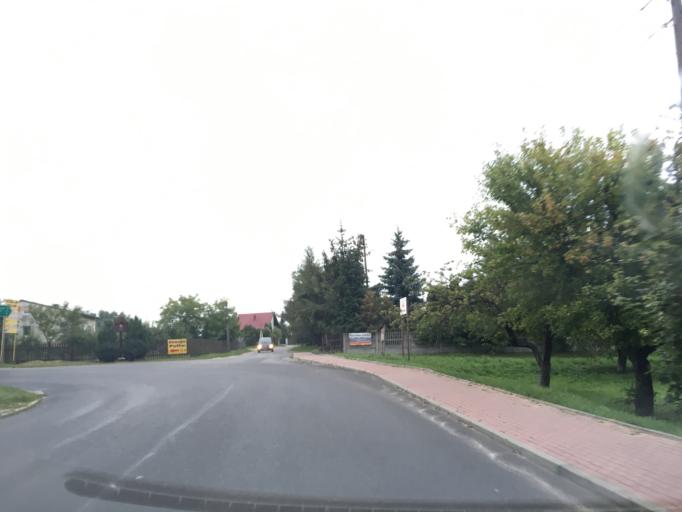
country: PL
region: Lodz Voivodeship
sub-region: Powiat piotrkowski
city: Leki Szlacheckie
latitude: 51.2095
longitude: 19.7250
